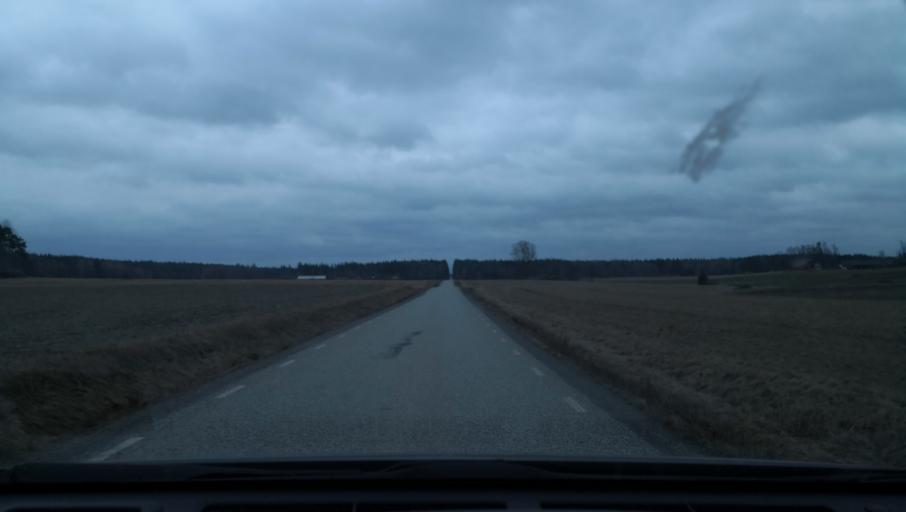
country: SE
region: OErebro
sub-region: Lindesbergs Kommun
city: Fellingsbro
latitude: 59.5609
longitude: 15.5853
